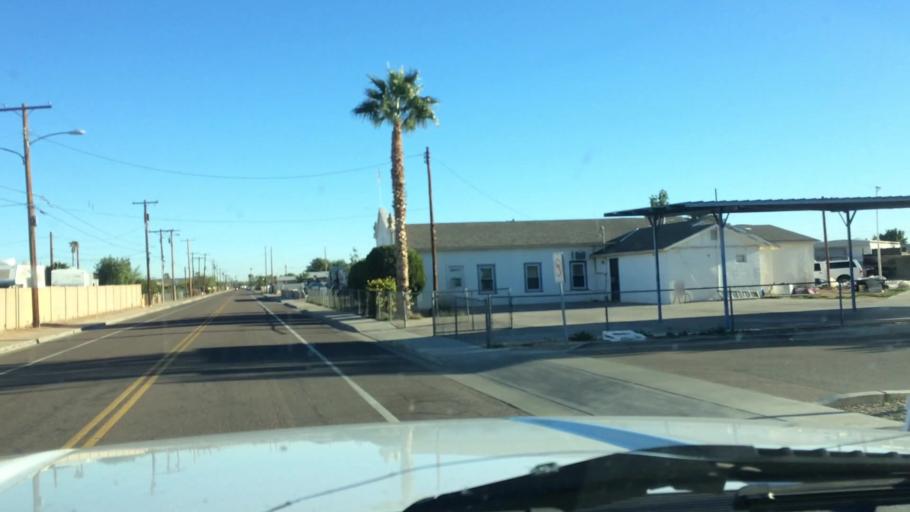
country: US
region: Arizona
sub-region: Maricopa County
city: Surprise
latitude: 33.6292
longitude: -112.3400
